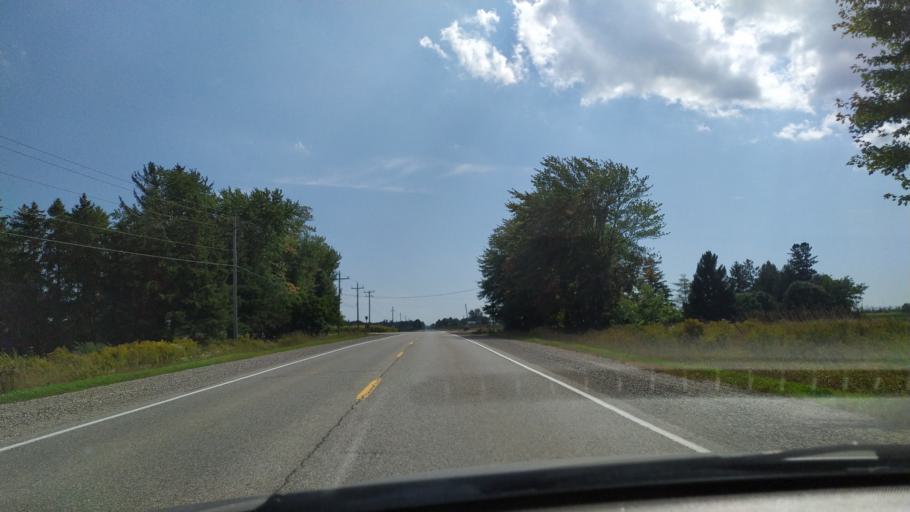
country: CA
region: Ontario
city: Ingersoll
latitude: 43.1247
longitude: -80.8858
